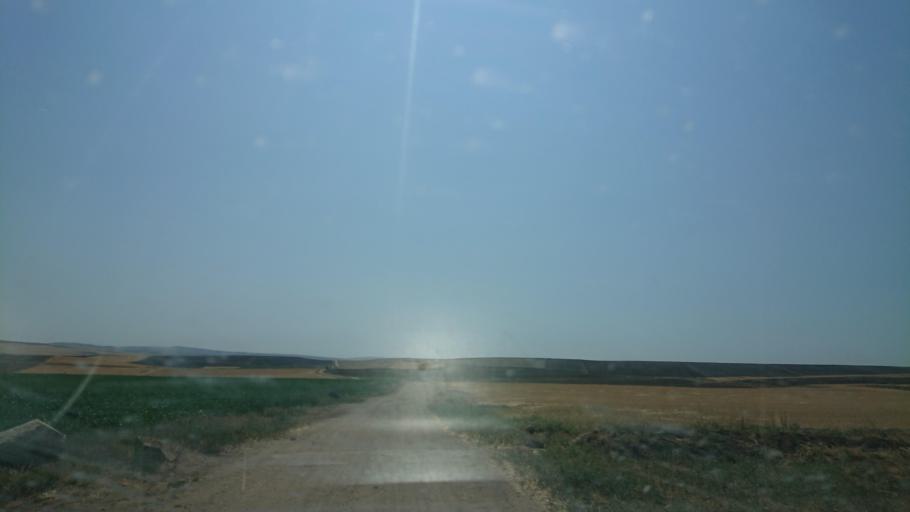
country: TR
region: Aksaray
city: Sariyahsi
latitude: 38.9567
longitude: 33.9138
